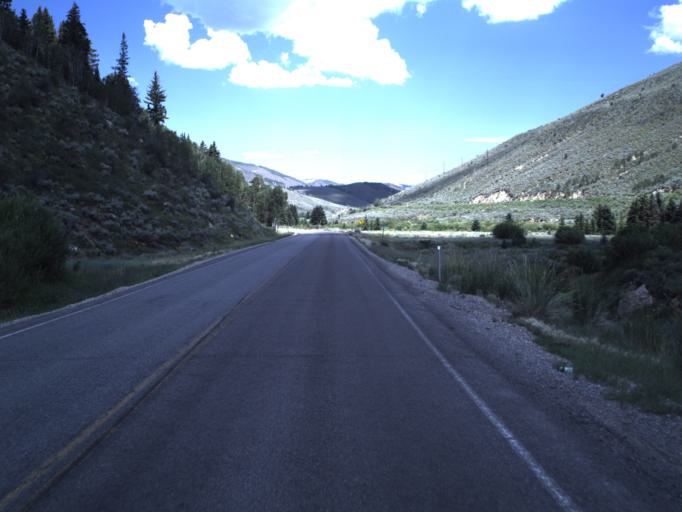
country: US
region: Utah
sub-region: Sanpete County
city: Fairview
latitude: 39.6980
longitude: -111.1577
